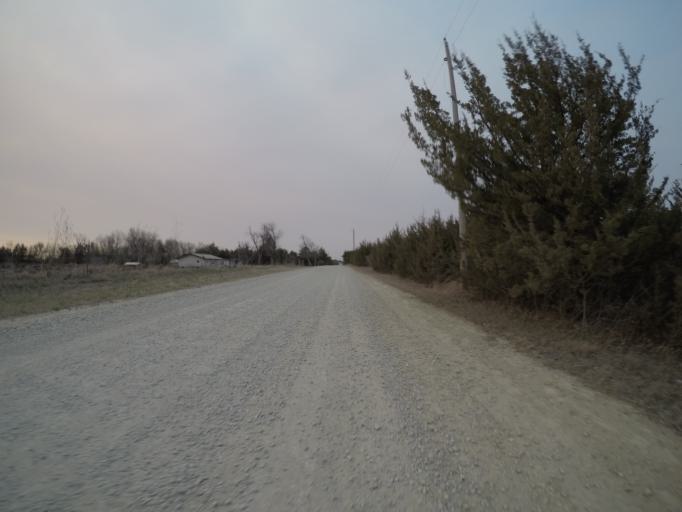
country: US
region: Kansas
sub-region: Riley County
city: Manhattan
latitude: 39.2420
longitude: -96.6538
